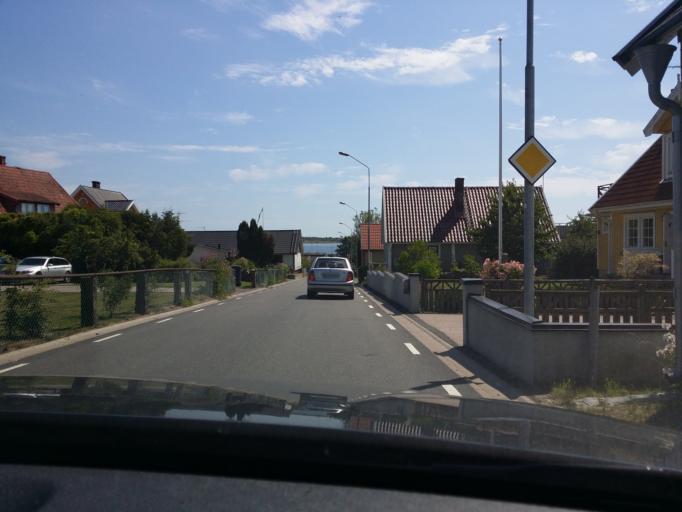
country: SE
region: Blekinge
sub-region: Solvesborgs Kommun
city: Soelvesborg
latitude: 56.0129
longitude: 14.6946
